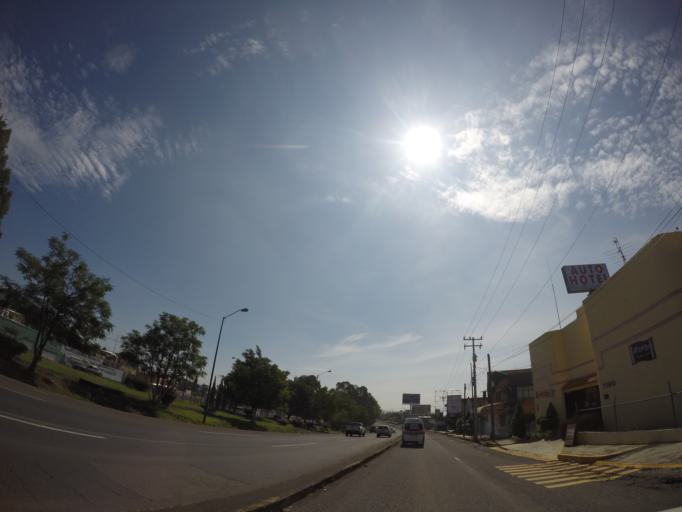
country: MX
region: Michoacan
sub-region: Morelia
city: San Antonio
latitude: 19.7061
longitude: -101.2393
